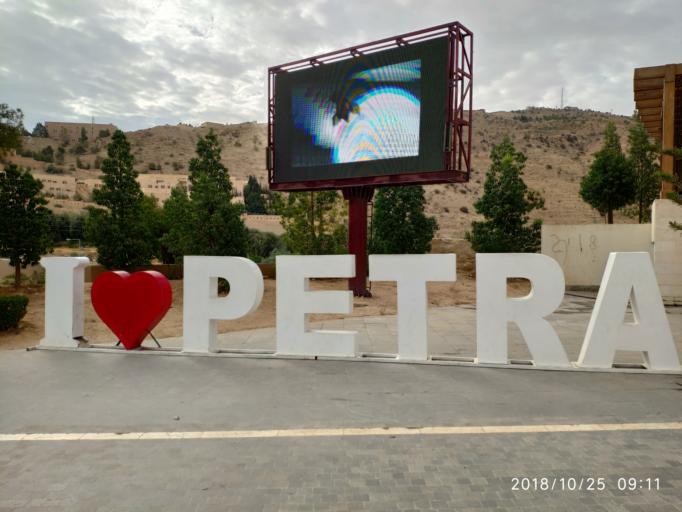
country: JO
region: Ma'an
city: Petra
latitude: 30.3248
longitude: 35.4682
